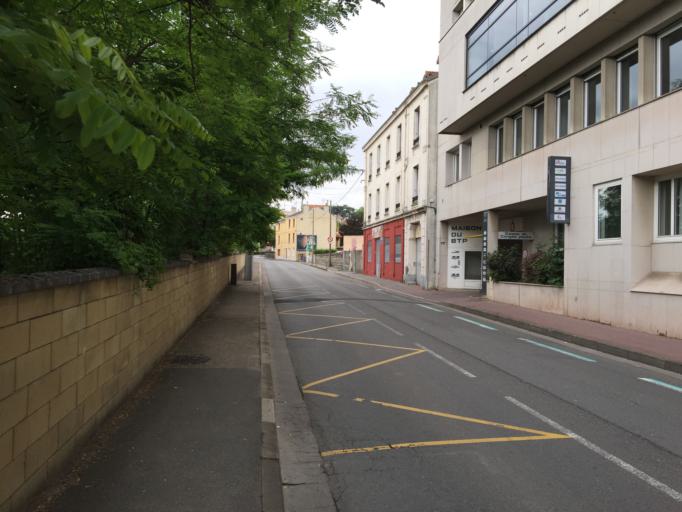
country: FR
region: Rhone-Alpes
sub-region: Departement de la Loire
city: Saint-Etienne
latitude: 45.4344
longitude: 4.3777
